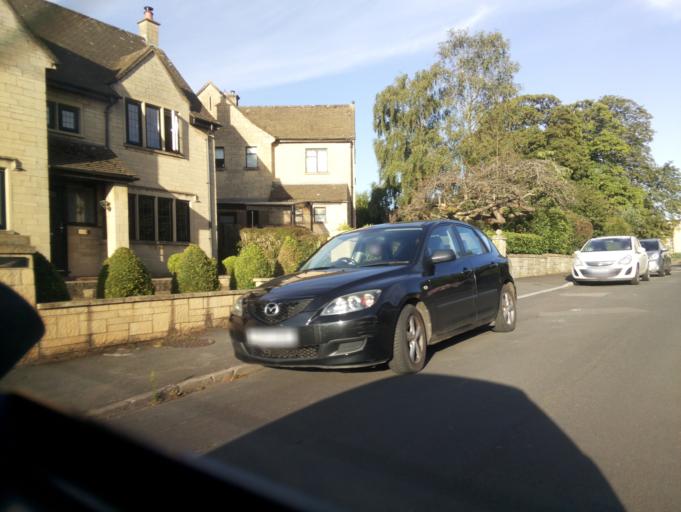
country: GB
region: England
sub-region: South Gloucestershire
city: Mangotsfield
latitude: 51.5007
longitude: -2.5169
